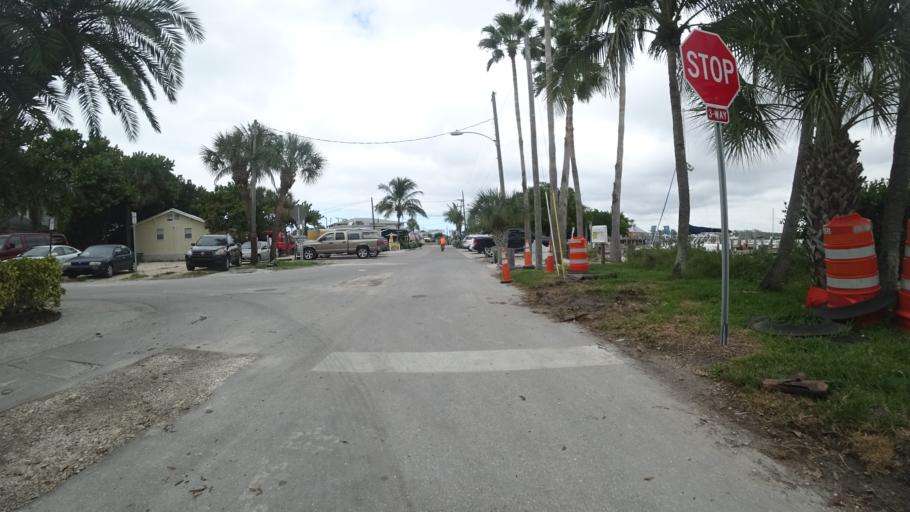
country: US
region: Florida
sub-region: Manatee County
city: Bradenton Beach
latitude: 27.4646
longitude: -82.6967
